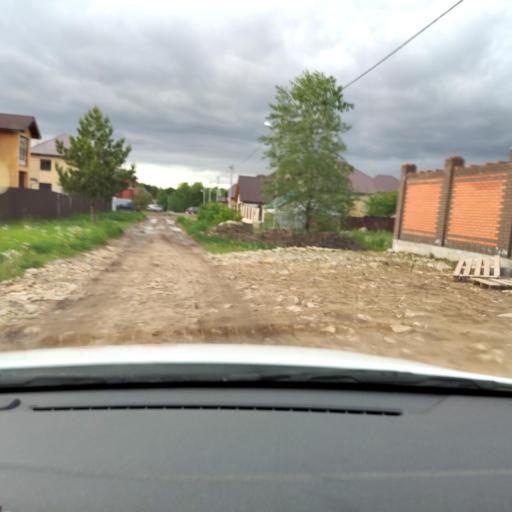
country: RU
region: Tatarstan
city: Vysokaya Gora
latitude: 55.7837
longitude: 49.2609
